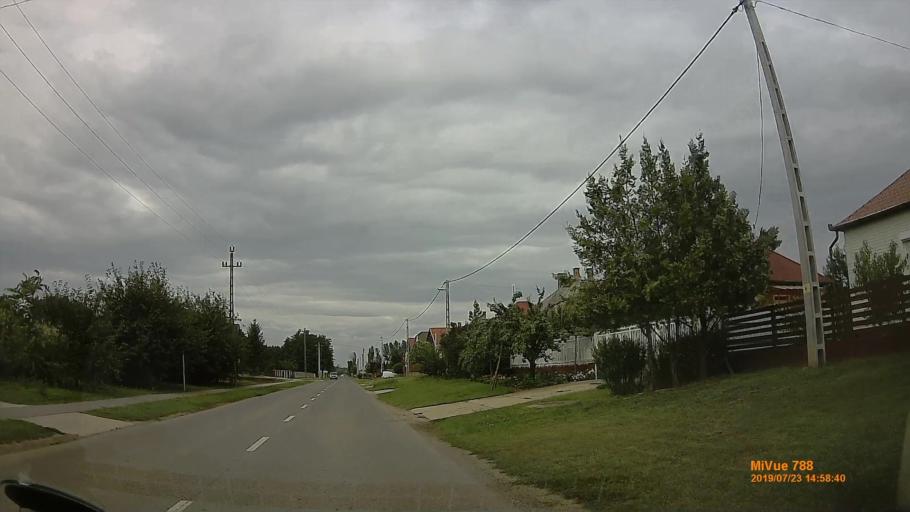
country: HU
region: Szabolcs-Szatmar-Bereg
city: Nyiregyhaza
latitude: 47.9147
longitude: 21.6757
